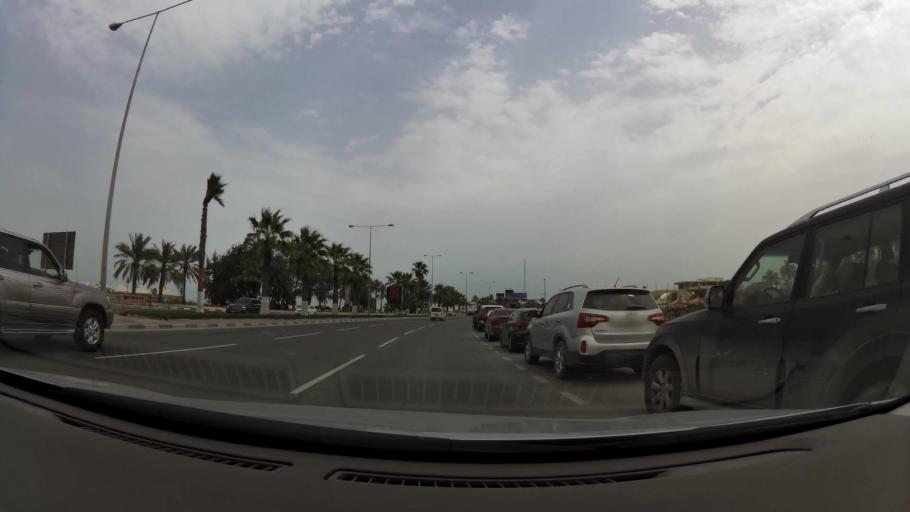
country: QA
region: Baladiyat ad Dawhah
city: Doha
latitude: 25.2912
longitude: 51.5475
